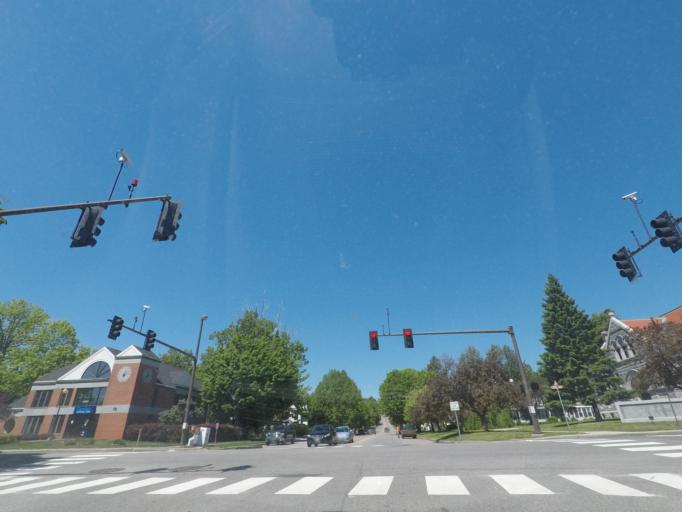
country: US
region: Maine
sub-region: Kennebec County
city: Augusta
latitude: 44.3151
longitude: -69.7773
